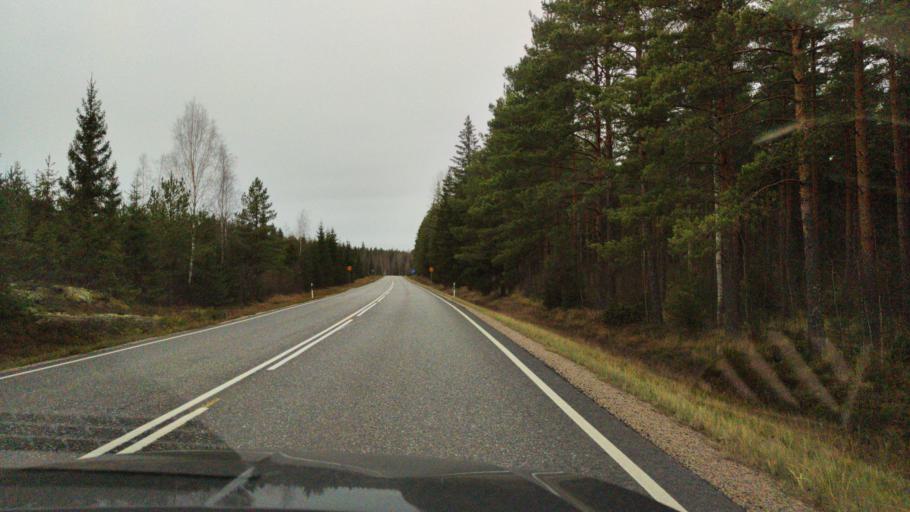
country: FI
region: Varsinais-Suomi
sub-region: Loimaa
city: Ylaene
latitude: 60.7359
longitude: 22.4322
